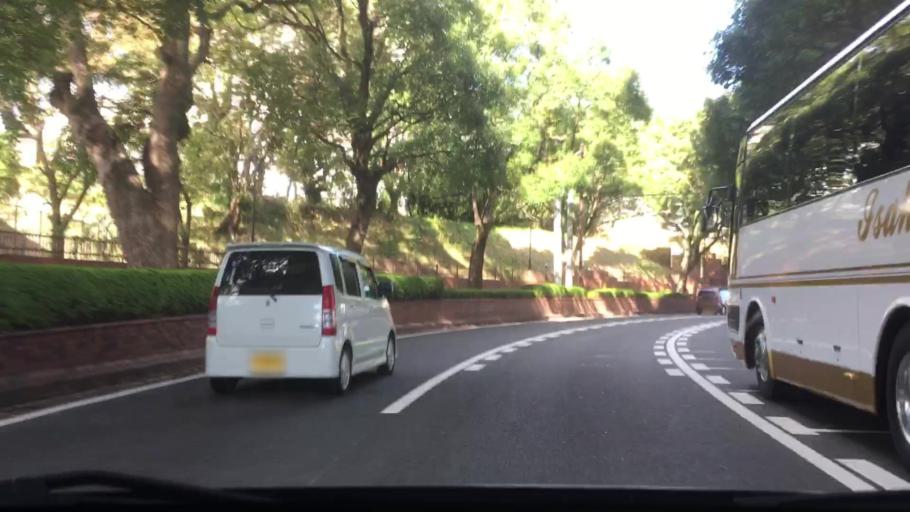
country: JP
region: Nagasaki
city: Sasebo
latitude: 33.1712
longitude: 129.7134
